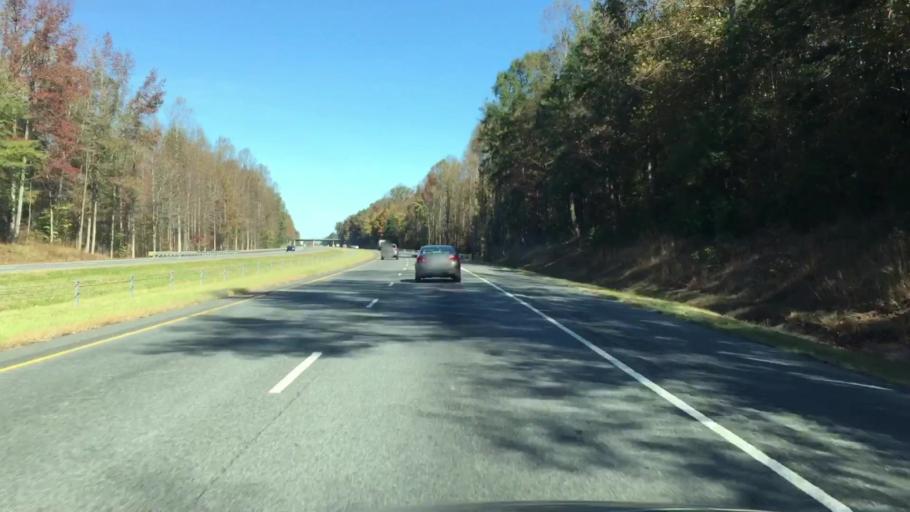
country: US
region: North Carolina
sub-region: Rockingham County
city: Reidsville
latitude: 36.2787
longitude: -79.6400
